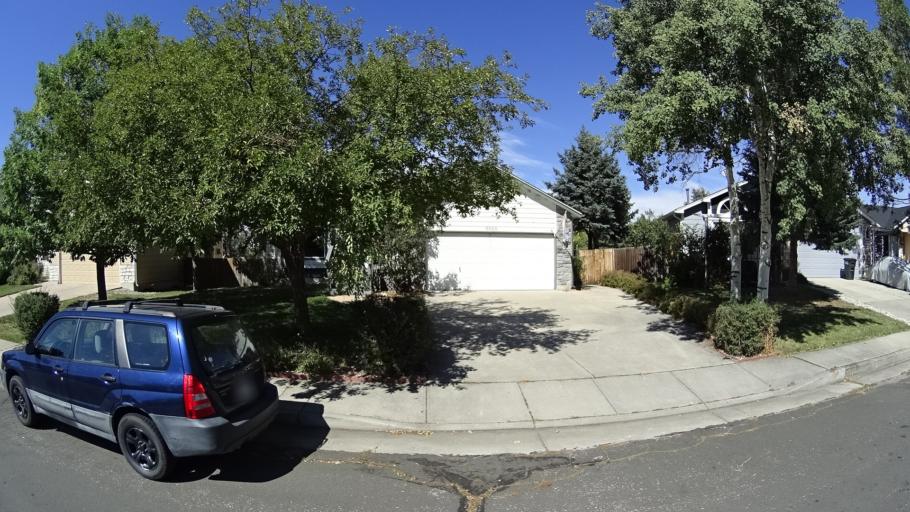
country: US
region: Colorado
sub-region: El Paso County
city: Cimarron Hills
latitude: 38.8979
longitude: -104.7062
